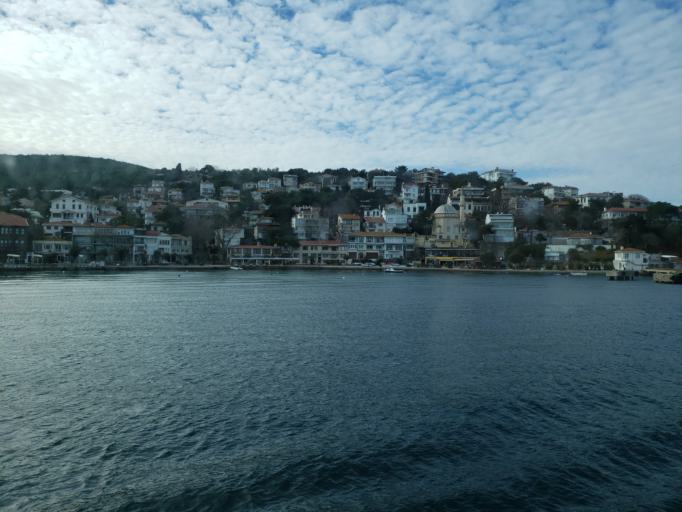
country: TR
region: Istanbul
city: Adalan
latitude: 40.8823
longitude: 29.0709
